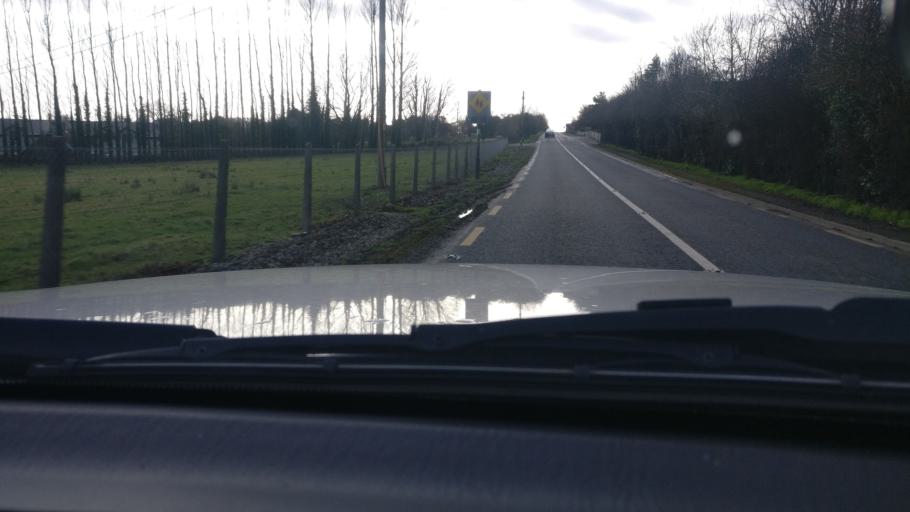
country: IE
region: Leinster
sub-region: An Iarmhi
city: Athlone
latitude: 53.4933
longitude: -7.8556
